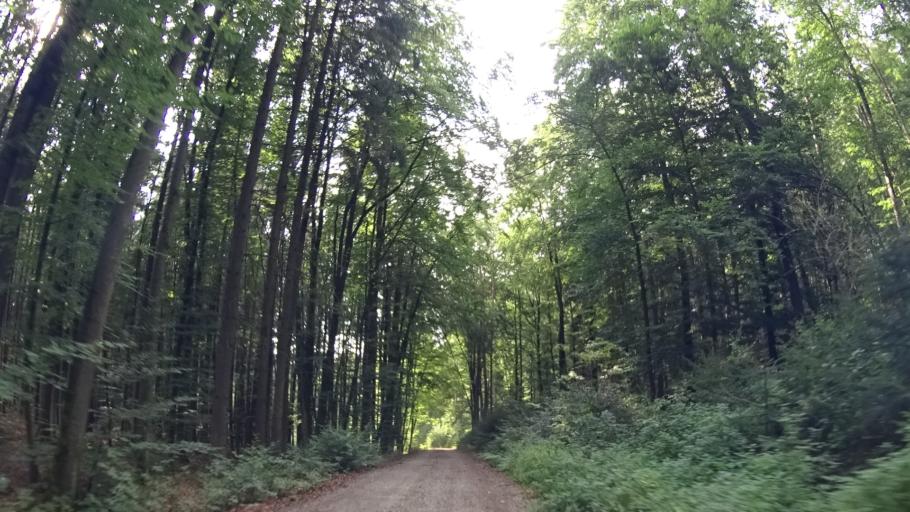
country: DE
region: Bavaria
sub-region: Lower Bavaria
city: Riedenburg
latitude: 48.9402
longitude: 11.6553
